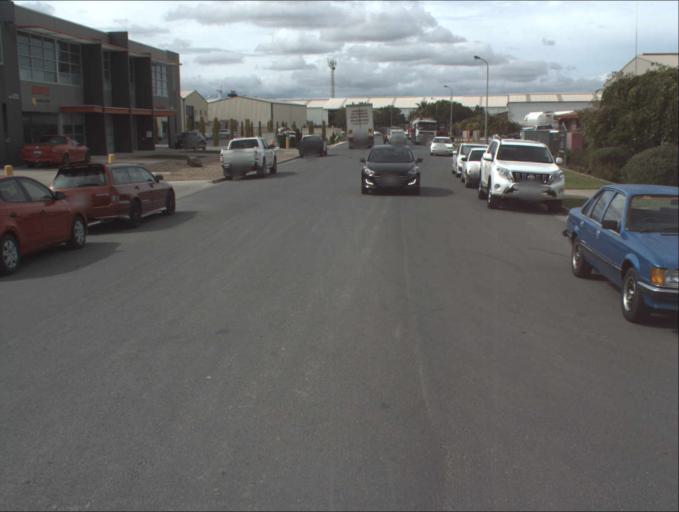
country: AU
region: South Australia
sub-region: Port Adelaide Enfield
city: Birkenhead
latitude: -34.8214
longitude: 138.5033
